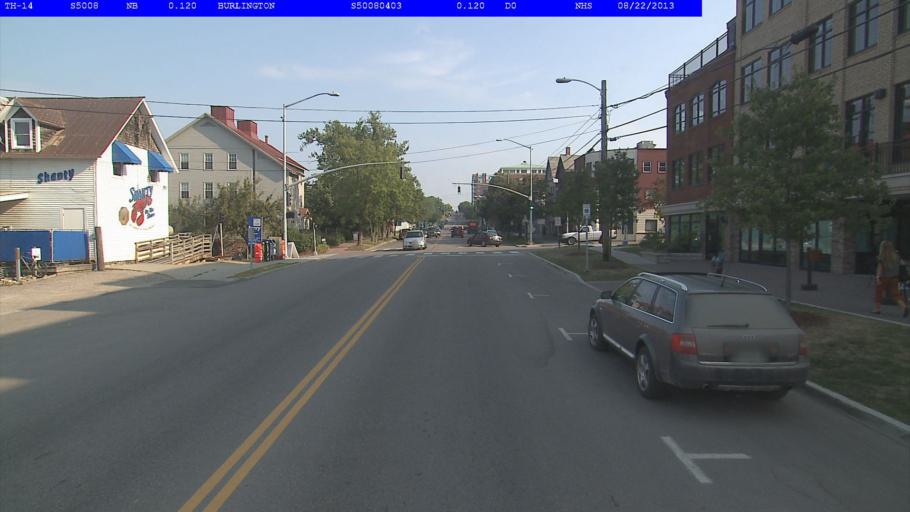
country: US
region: Vermont
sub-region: Chittenden County
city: Burlington
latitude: 44.4741
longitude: -73.2185
